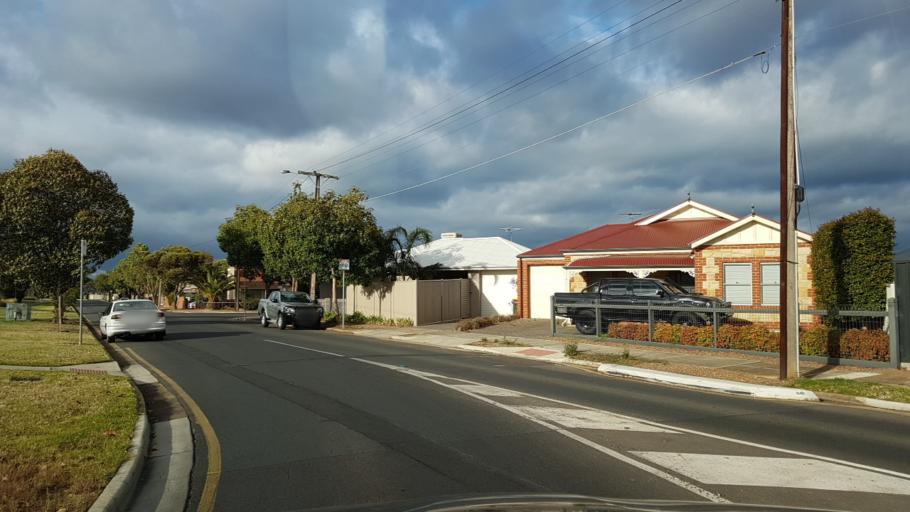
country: AU
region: South Australia
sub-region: City of West Torrens
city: Plympton
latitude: -34.9544
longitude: 138.5587
